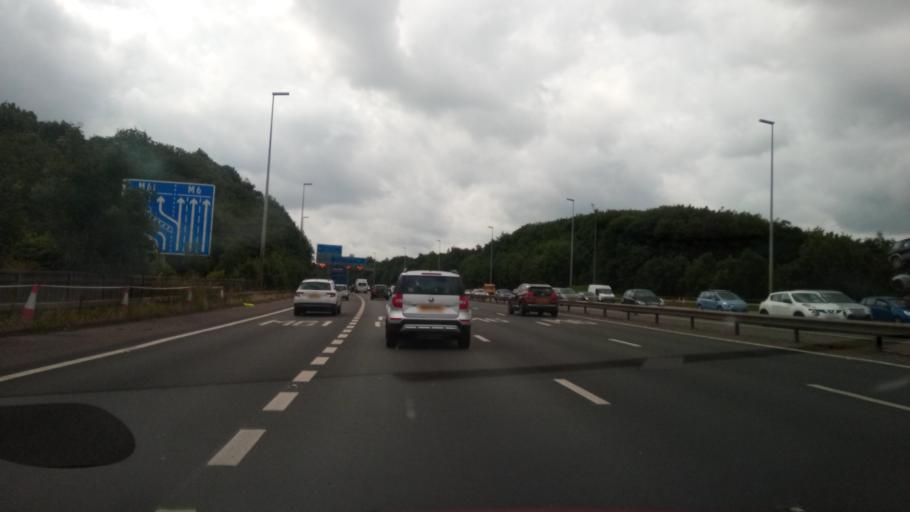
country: GB
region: England
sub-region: Lancashire
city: Clayton-le-Woods
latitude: 53.7435
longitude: -2.6504
